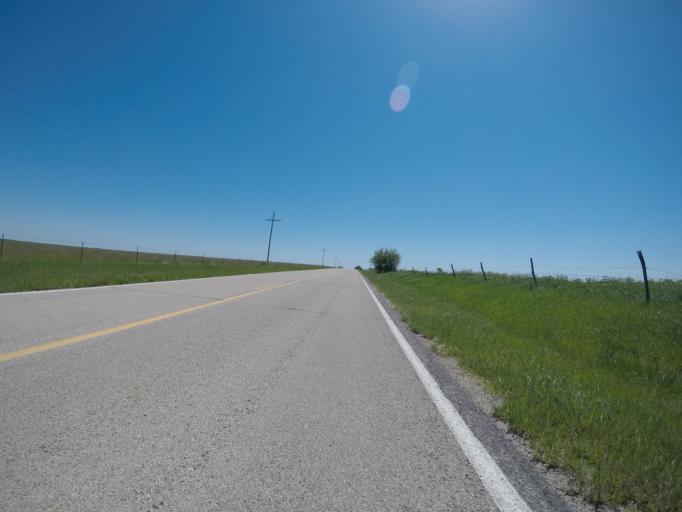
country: US
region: Kansas
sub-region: Shawnee County
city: Auburn
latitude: 38.8847
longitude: -95.9872
